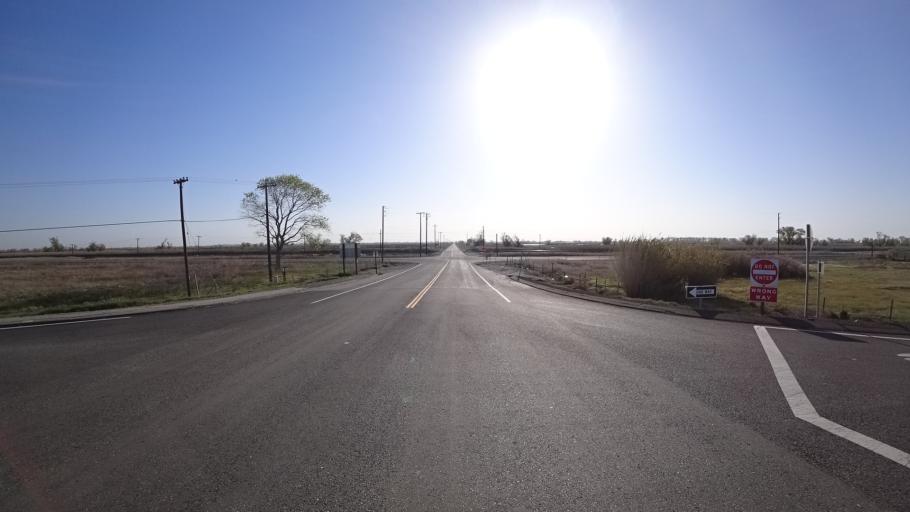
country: US
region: California
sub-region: Glenn County
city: Willows
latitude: 39.4071
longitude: -122.1938
